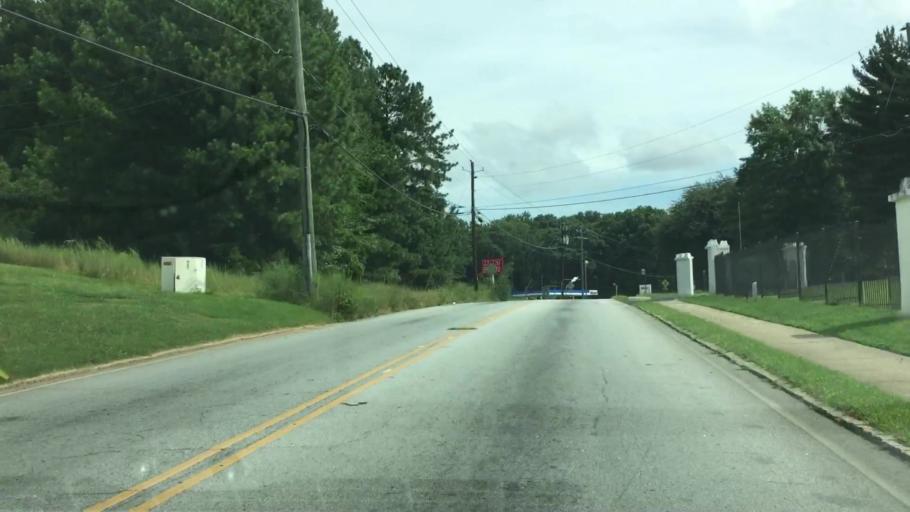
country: US
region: Georgia
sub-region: DeKalb County
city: Gresham Park
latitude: 33.7175
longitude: -84.3426
